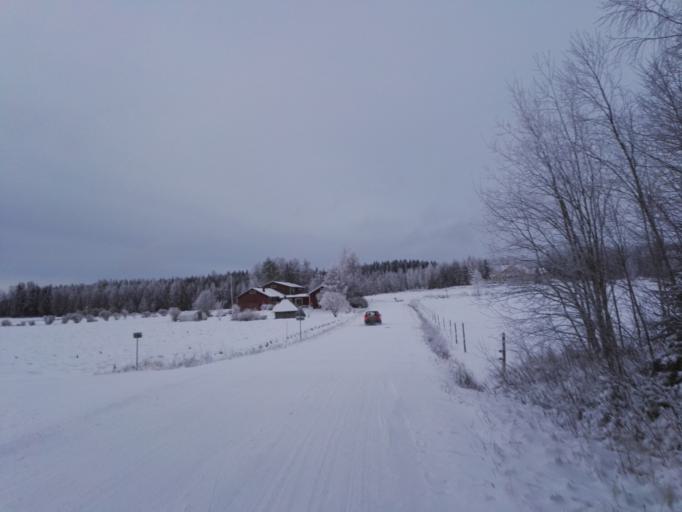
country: FI
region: Satakunta
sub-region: Pohjois-Satakunta
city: Jaemijaervi
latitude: 61.7805
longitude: 22.8762
